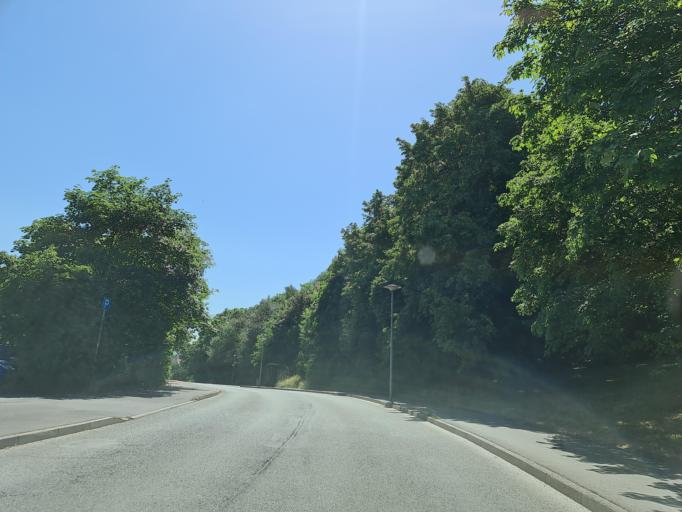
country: DE
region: Saxony
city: Plauen
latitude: 50.5043
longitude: 12.1291
